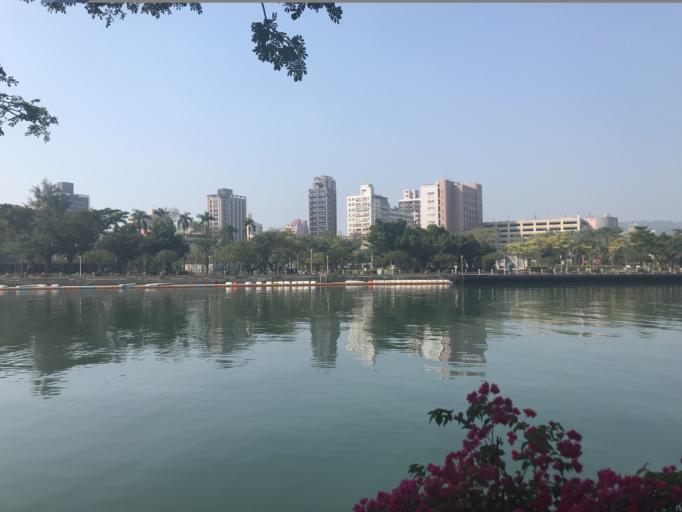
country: TW
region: Kaohsiung
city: Kaohsiung
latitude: 22.6242
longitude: 120.2900
